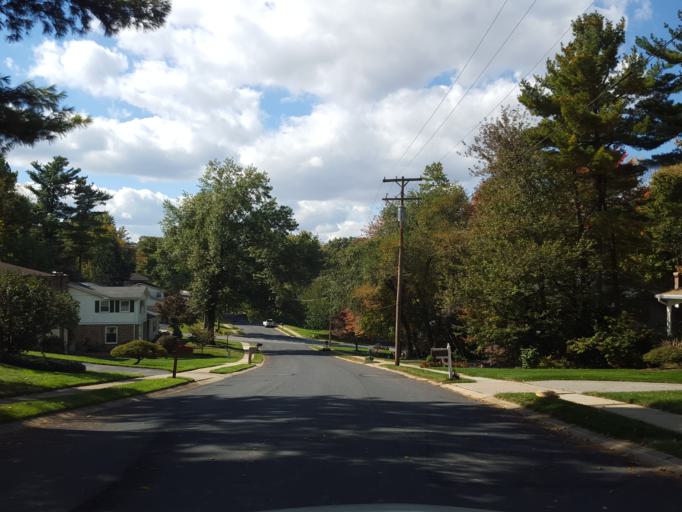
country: US
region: Pennsylvania
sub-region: York County
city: East York
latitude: 39.9649
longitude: -76.6639
